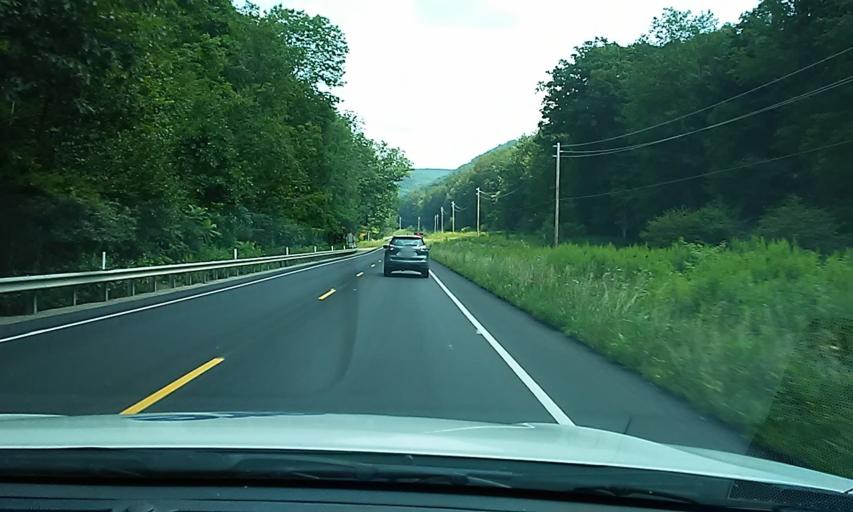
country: US
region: Pennsylvania
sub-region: Elk County
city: Saint Marys
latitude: 41.4702
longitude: -78.4053
